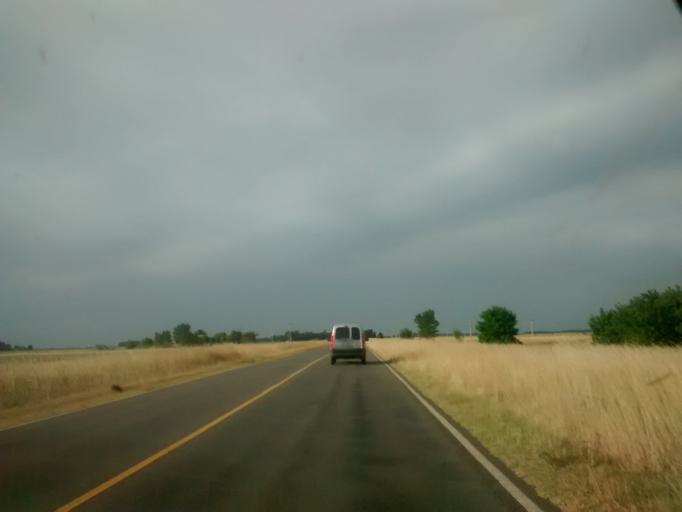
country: AR
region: Buenos Aires
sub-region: Partido de Ayacucho
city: Ayacucho
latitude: -36.6441
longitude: -58.5734
